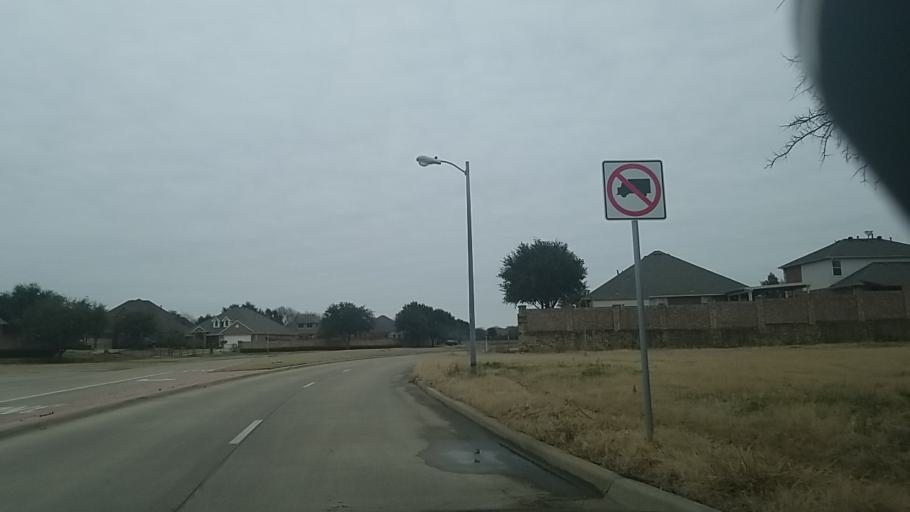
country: US
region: Texas
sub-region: Denton County
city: Corinth
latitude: 33.1299
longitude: -97.0745
